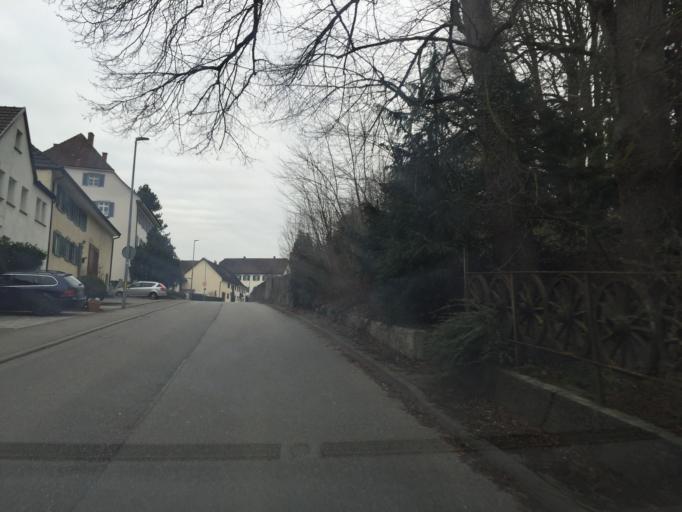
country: DE
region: Baden-Wuerttemberg
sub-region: Freiburg Region
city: Gailingen
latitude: 47.7217
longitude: 8.7510
